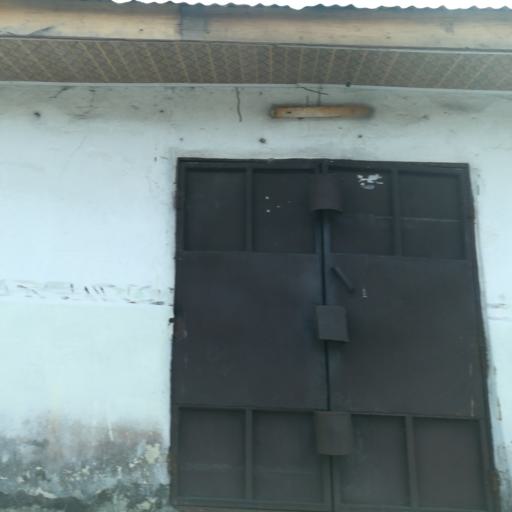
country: NG
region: Rivers
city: Port Harcourt
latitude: 4.7816
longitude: 7.0365
